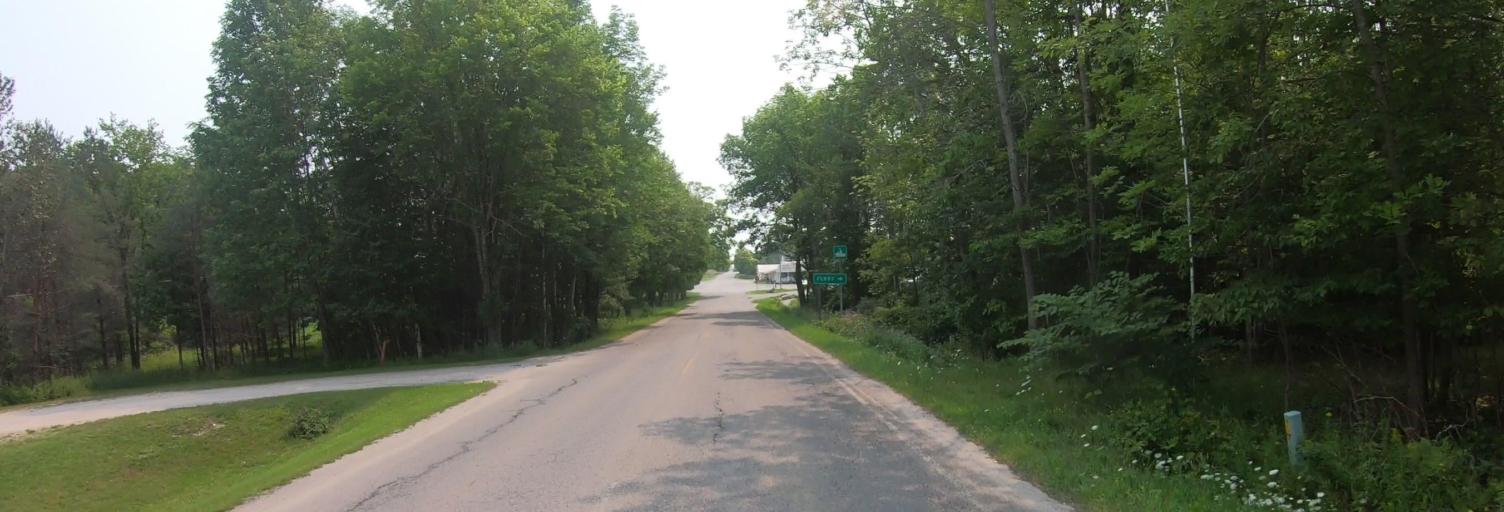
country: CA
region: Ontario
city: Thessalon
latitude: 46.0003
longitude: -83.7387
